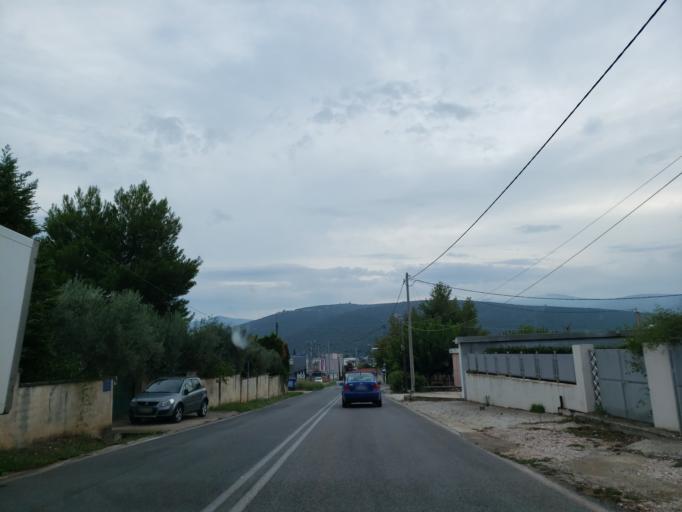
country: GR
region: Attica
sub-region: Nomarchia Anatolikis Attikis
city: Marathonas
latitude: 38.1611
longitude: 23.9618
